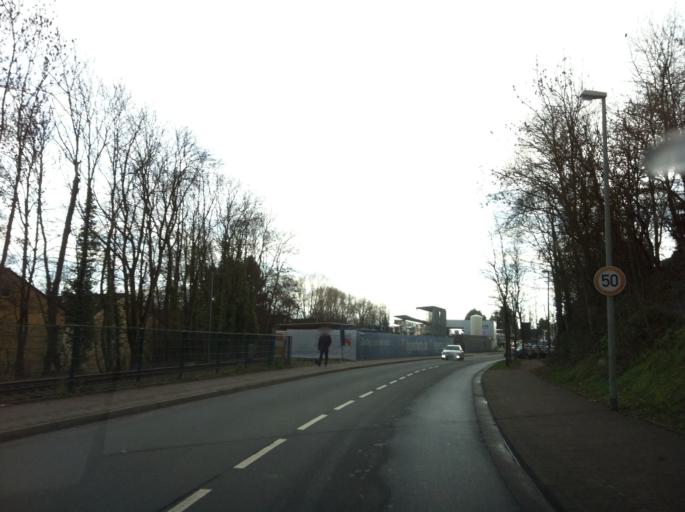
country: DE
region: Hesse
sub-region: Regierungsbezirk Darmstadt
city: Kronberg
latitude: 50.1796
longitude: 8.5181
